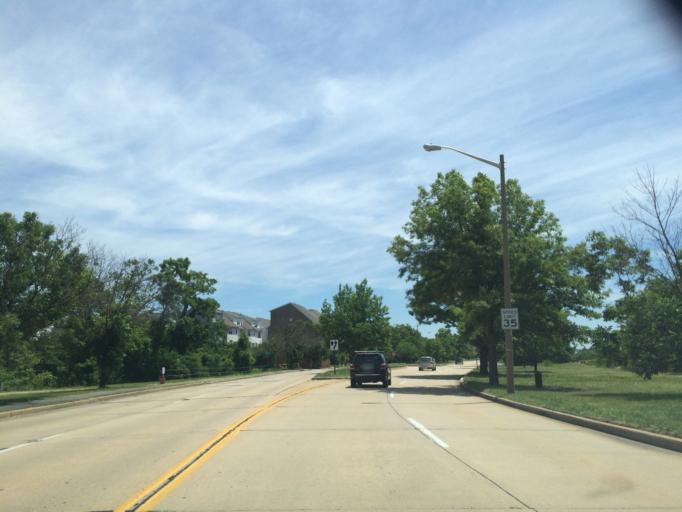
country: US
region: Virginia
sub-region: Fairfax County
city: Rose Hill
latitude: 38.8041
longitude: -77.0985
